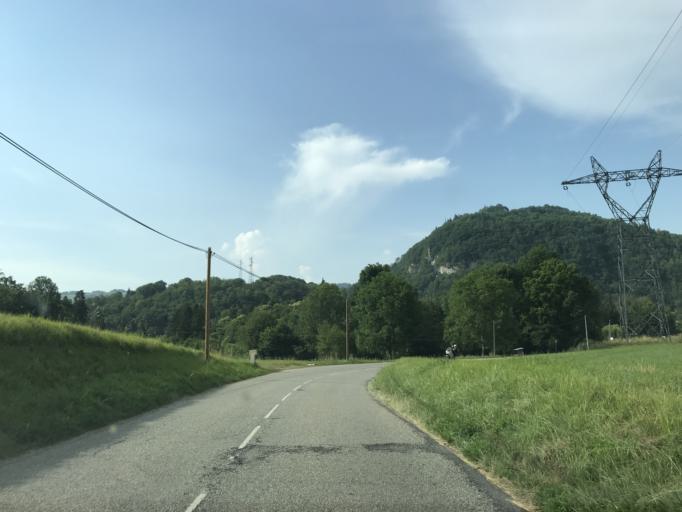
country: FR
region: Rhone-Alpes
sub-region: Departement de la Savoie
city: La Rochette
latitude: 45.4283
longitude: 6.0996
